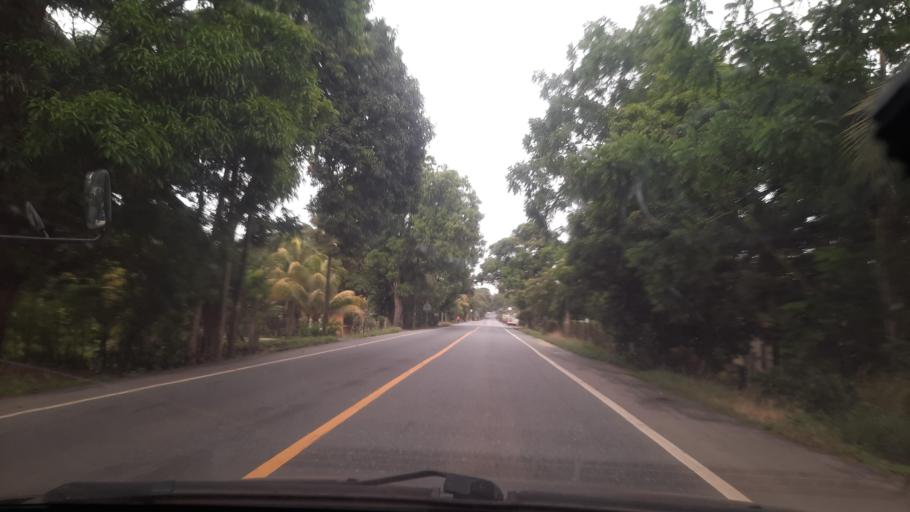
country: GT
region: Izabal
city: Morales
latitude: 15.4433
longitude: -88.9488
